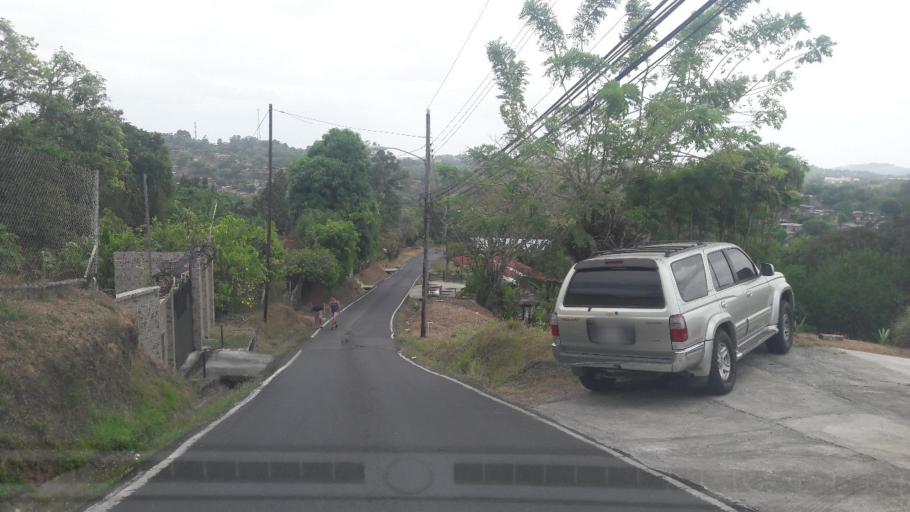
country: PA
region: Panama
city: Alcalde Diaz
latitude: 9.1245
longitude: -79.5498
